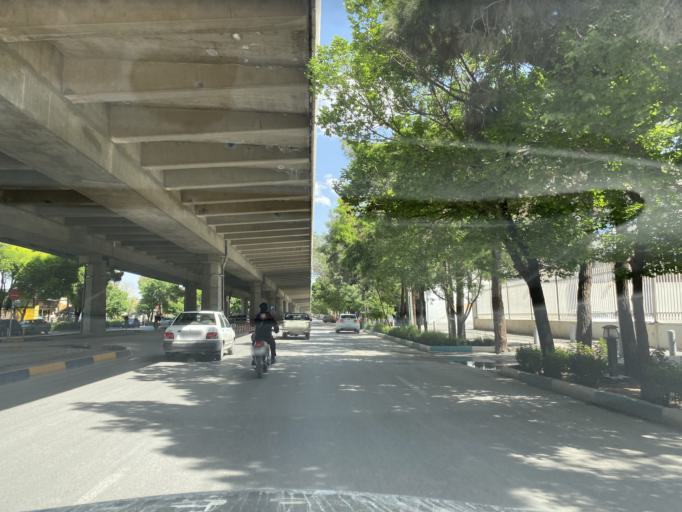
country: IR
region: Isfahan
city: Rehnan
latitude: 32.6895
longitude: 51.6310
